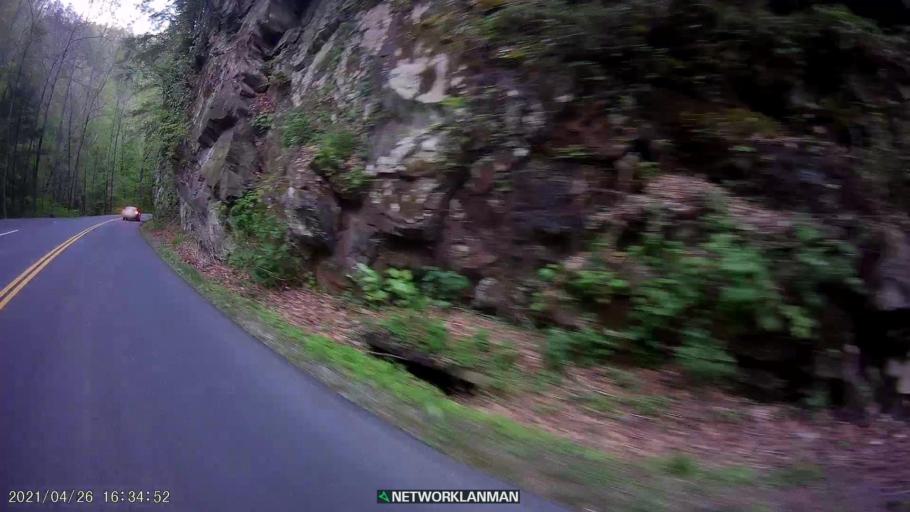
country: US
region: Tennessee
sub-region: Sevier County
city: Pigeon Forge
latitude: 35.6484
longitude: -83.7147
